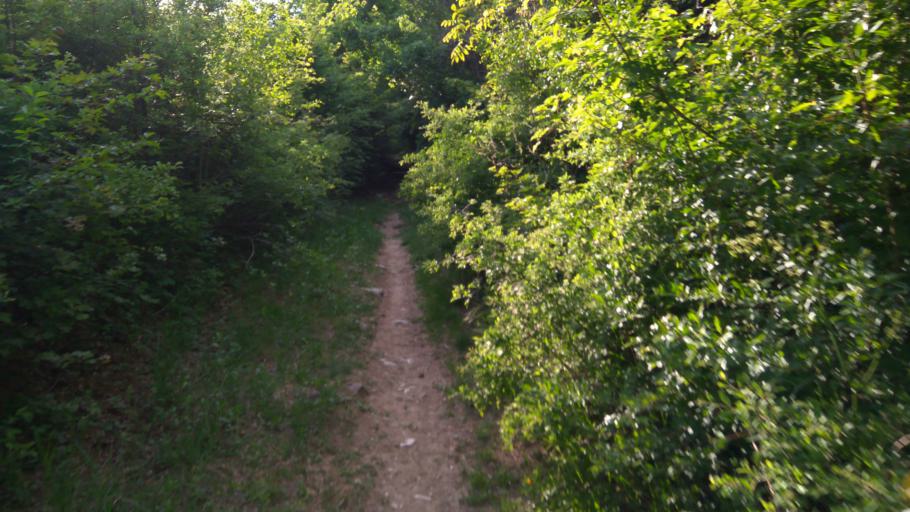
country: HU
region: Pest
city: Csobanka
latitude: 47.6517
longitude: 18.9843
